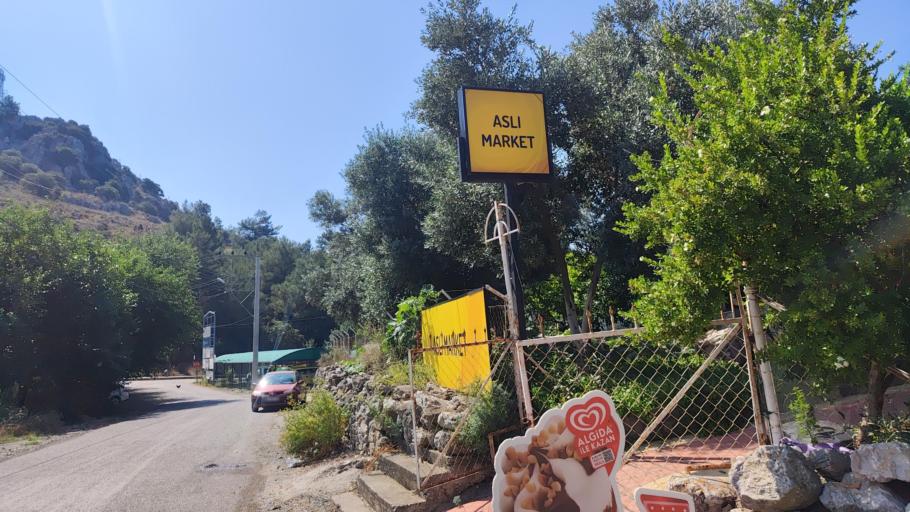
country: TR
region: Mugla
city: Sarigerme
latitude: 36.7085
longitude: 28.6980
